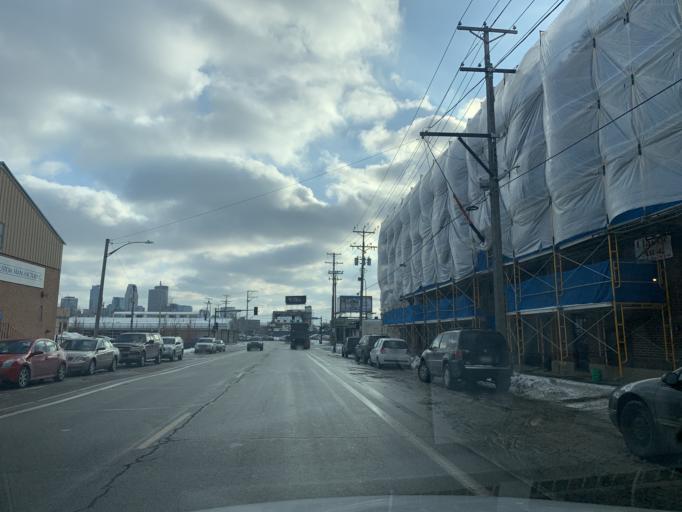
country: US
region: Minnesota
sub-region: Hennepin County
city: Minneapolis
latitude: 45.0001
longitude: -93.2801
